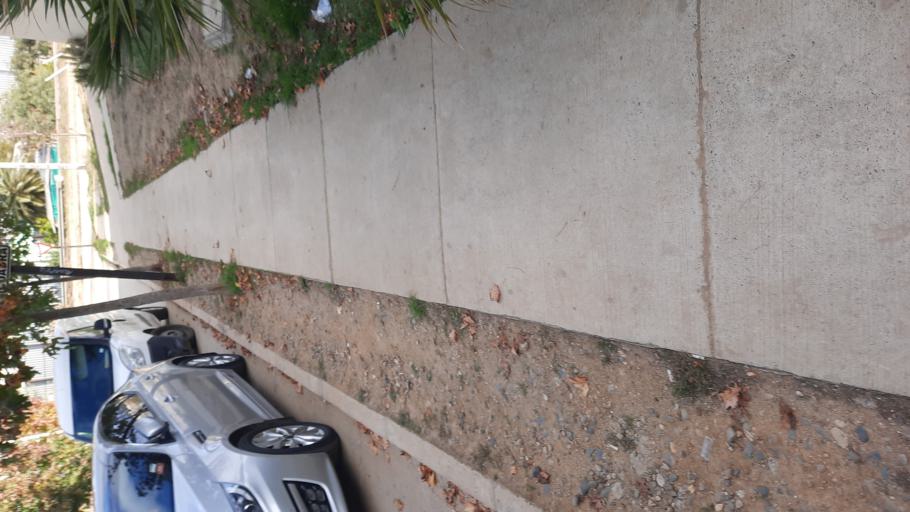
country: CL
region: Valparaiso
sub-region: Provincia de Valparaiso
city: Vina del Mar
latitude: -33.1138
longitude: -71.5529
